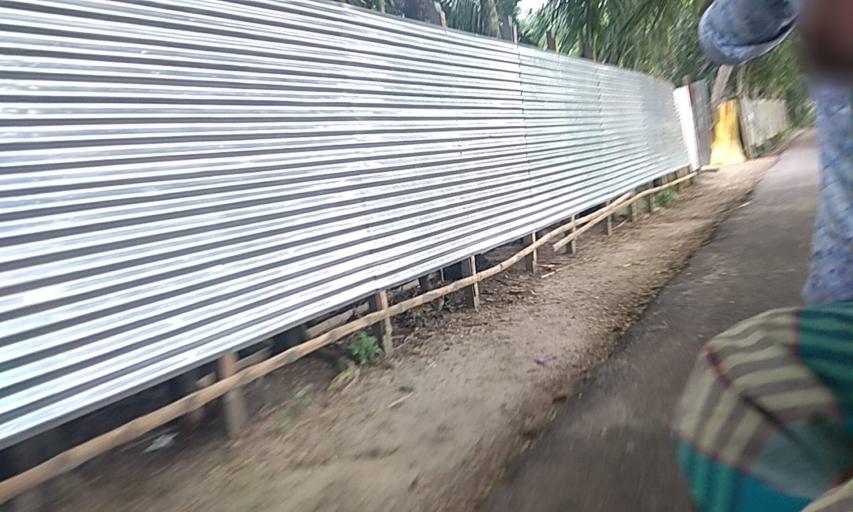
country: BD
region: Dhaka
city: Dohar
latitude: 23.4755
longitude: 90.0528
